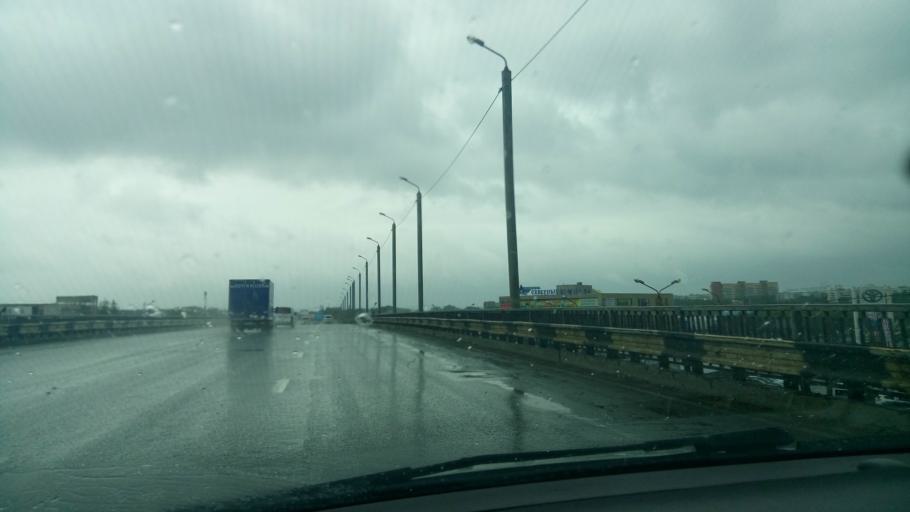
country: RU
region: Chelyabinsk
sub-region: Gorod Chelyabinsk
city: Chelyabinsk
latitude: 55.2277
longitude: 61.3744
